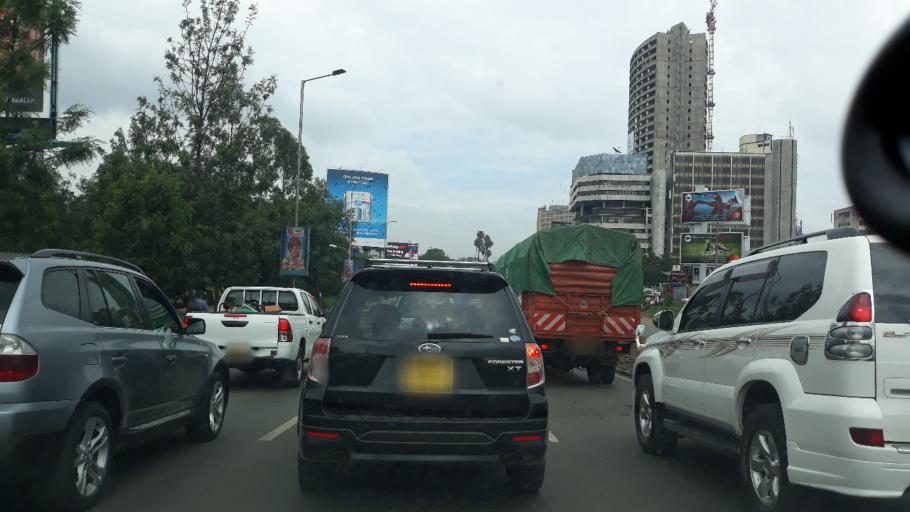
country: KE
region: Nairobi Area
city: Nairobi
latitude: -1.2944
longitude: 36.8213
